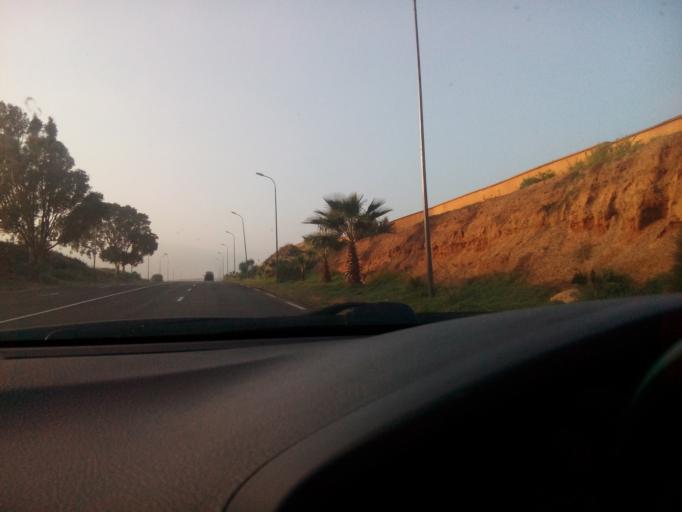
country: DZ
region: Oran
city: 'Ain el Turk
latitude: 35.7158
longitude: -0.8536
